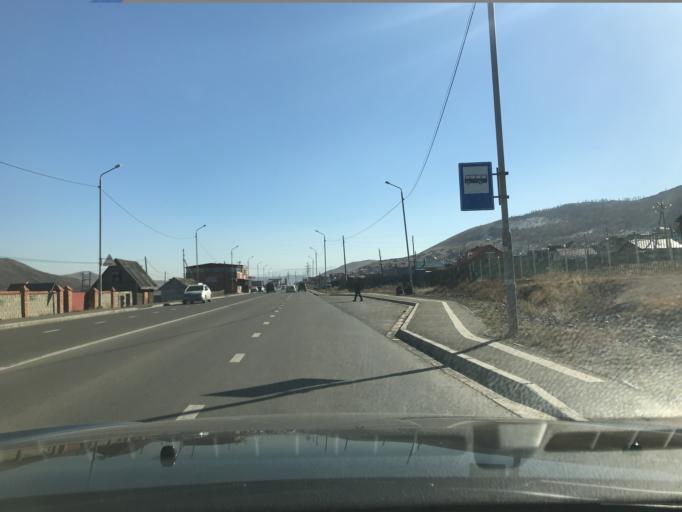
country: MN
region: Ulaanbaatar
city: Ulaanbaatar
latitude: 48.0393
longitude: 106.9051
